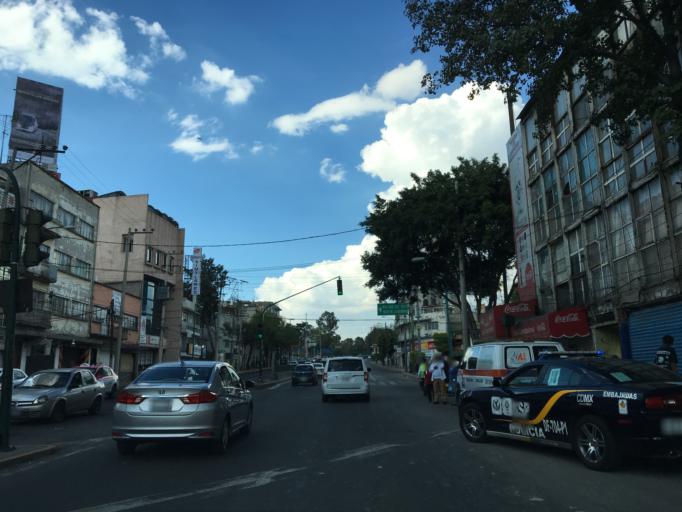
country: MX
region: Mexico City
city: Polanco
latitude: 19.4101
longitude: -99.1906
